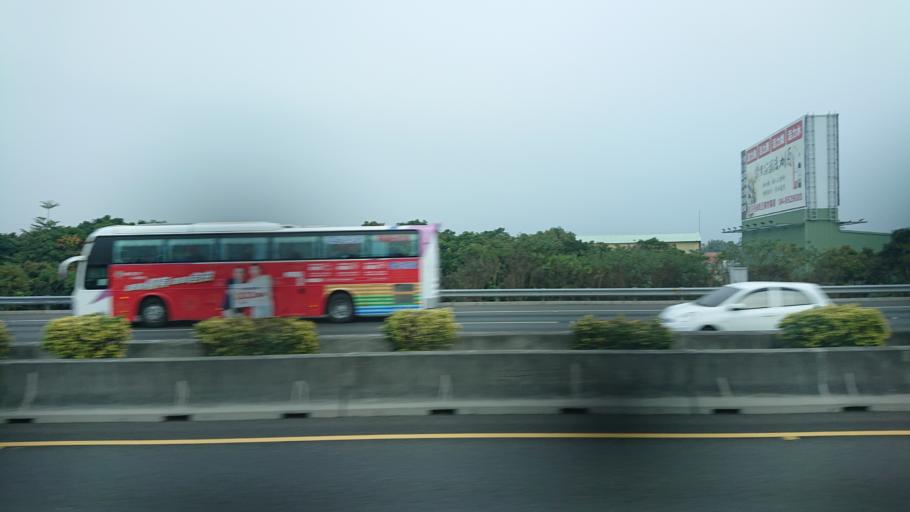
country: TW
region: Taiwan
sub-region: Nantou
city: Nantou
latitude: 23.9047
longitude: 120.4978
